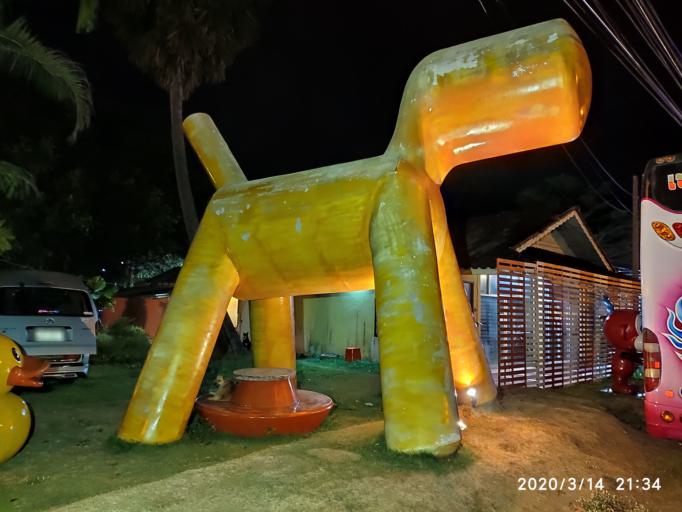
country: TH
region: Rayong
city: Klaeng
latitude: 12.6319
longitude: 101.4922
